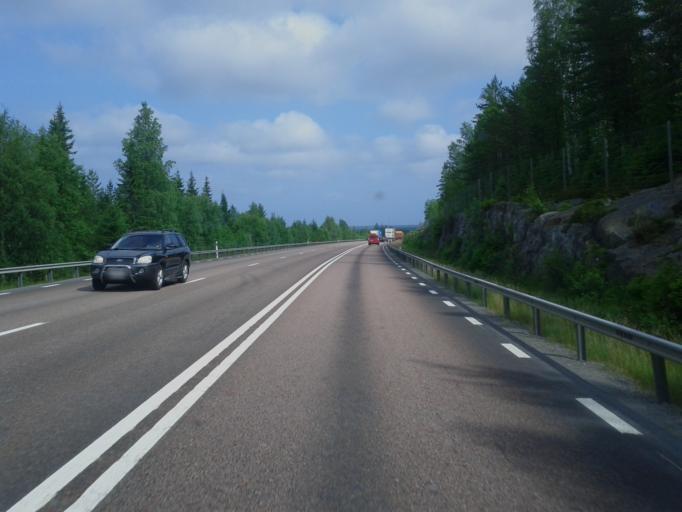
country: SE
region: Vaesterbotten
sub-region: Skelleftea Kommun
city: Burea
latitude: 64.4523
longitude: 21.2848
